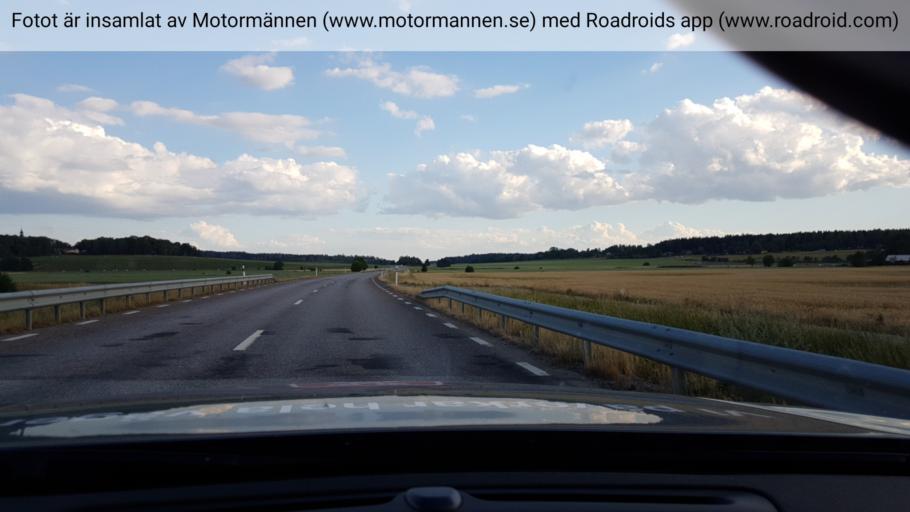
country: SE
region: Uppsala
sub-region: Heby Kommun
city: Morgongava
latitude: 59.8291
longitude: 16.9269
